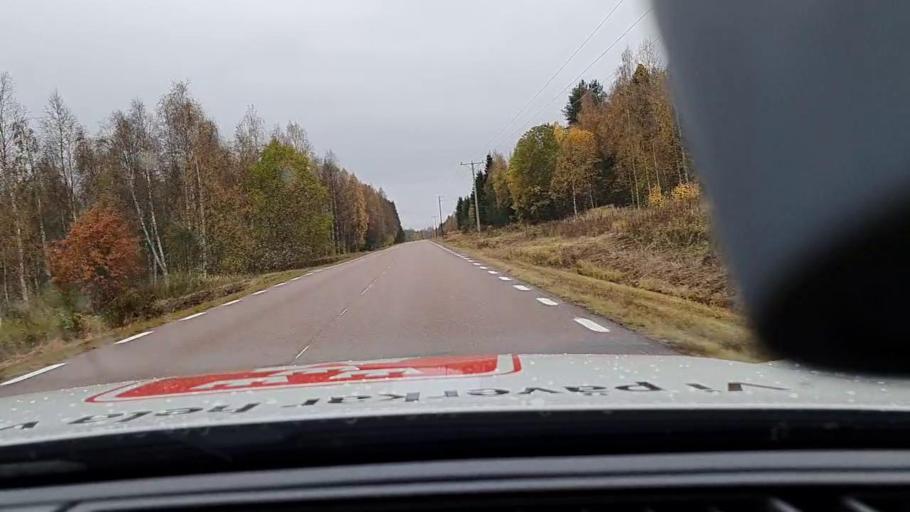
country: FI
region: Lapland
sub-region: Torniolaakso
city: Ylitornio
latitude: 66.1258
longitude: 23.9120
